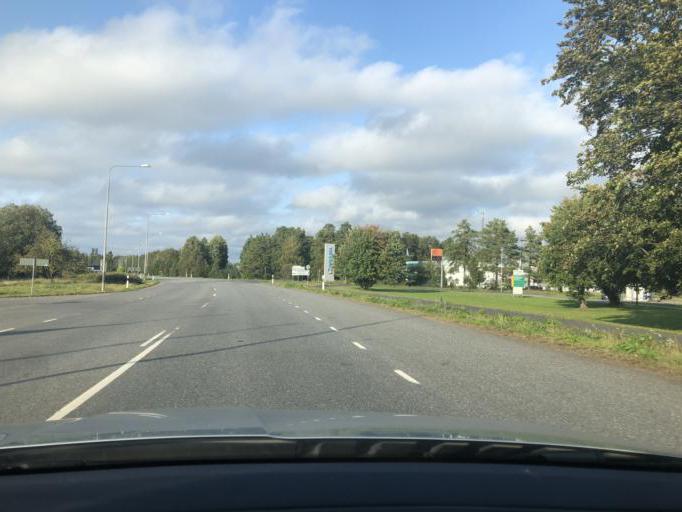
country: SE
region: Joenkoeping
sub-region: Varnamo Kommun
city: Varnamo
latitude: 57.2081
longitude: 14.0386
